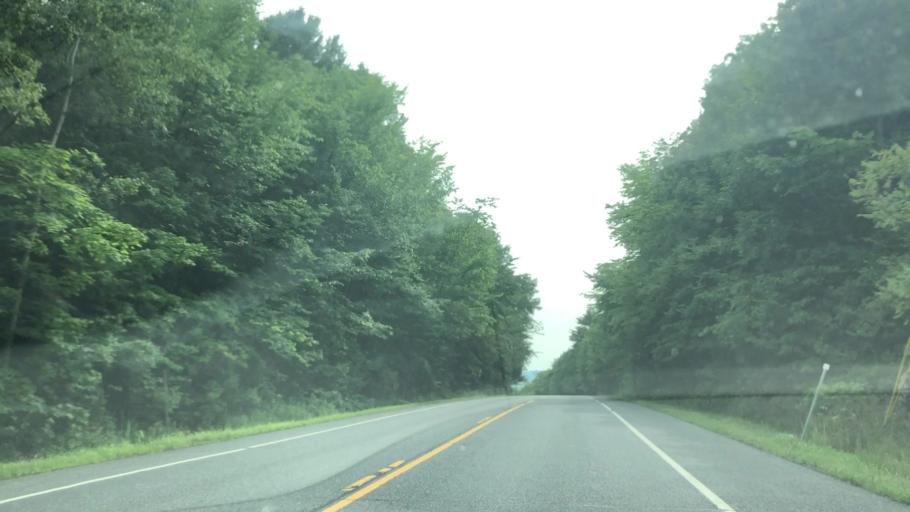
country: US
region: Vermont
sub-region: Rutland County
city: Fair Haven
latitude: 43.5661
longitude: -73.3273
